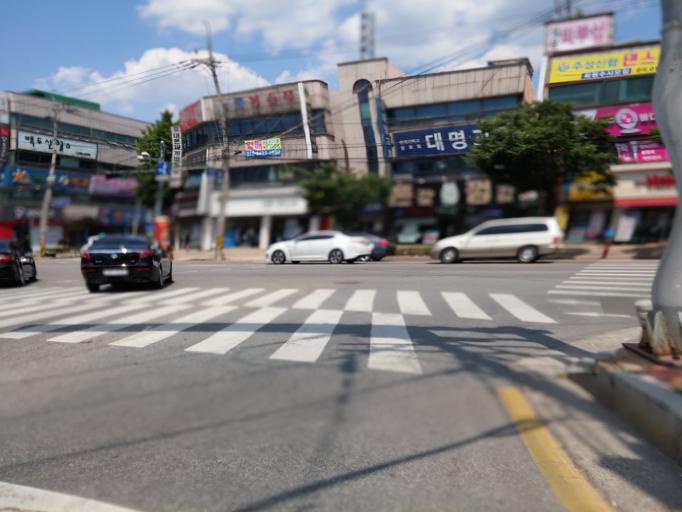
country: KR
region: Chungcheongbuk-do
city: Cheongju-si
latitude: 36.6287
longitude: 127.4406
